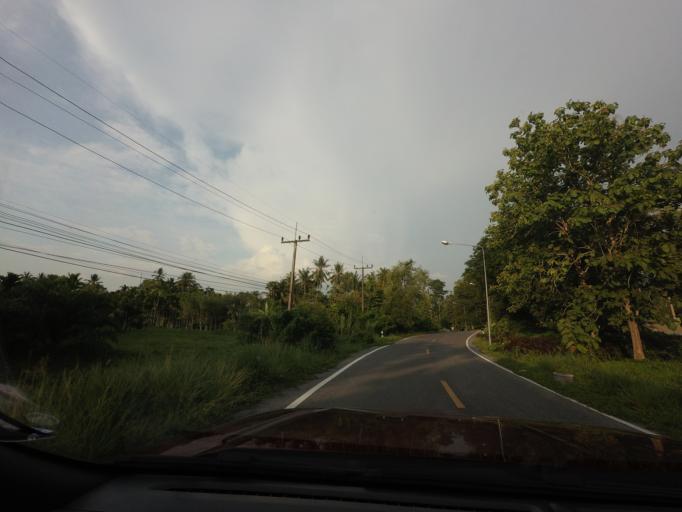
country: TH
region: Pattani
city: Khok Pho
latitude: 6.6702
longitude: 101.1028
